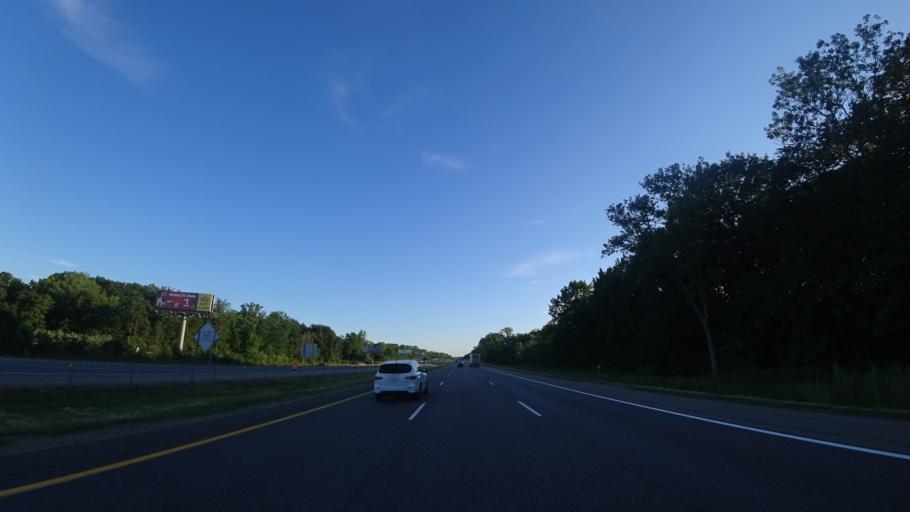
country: US
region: Michigan
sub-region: Berrien County
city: Bridgman
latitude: 41.9119
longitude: -86.5789
